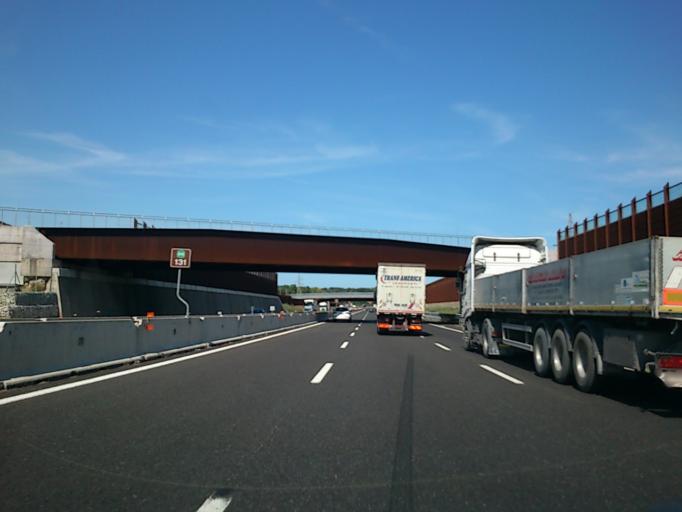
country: IT
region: The Marches
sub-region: Provincia di Pesaro e Urbino
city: Centinarola
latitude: 43.8275
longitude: 12.9968
